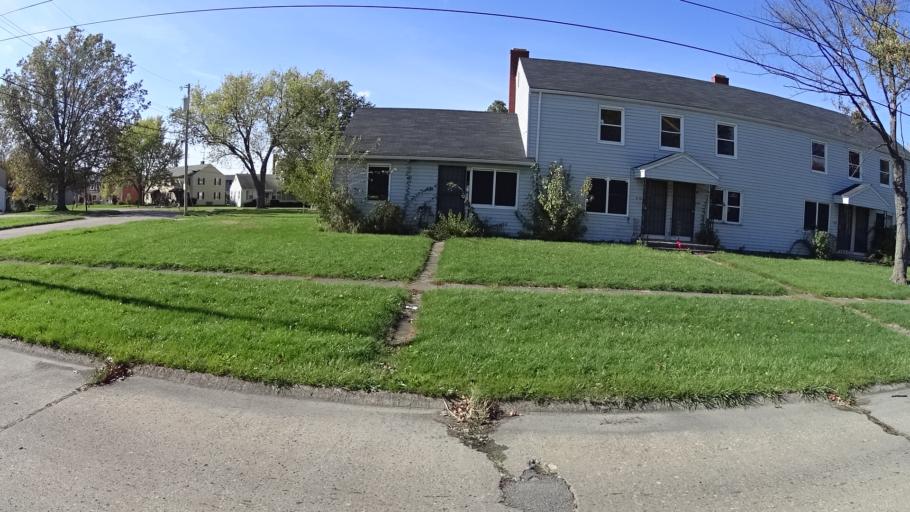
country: US
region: Ohio
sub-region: Lorain County
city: Lorain
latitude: 41.4478
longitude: -82.1769
